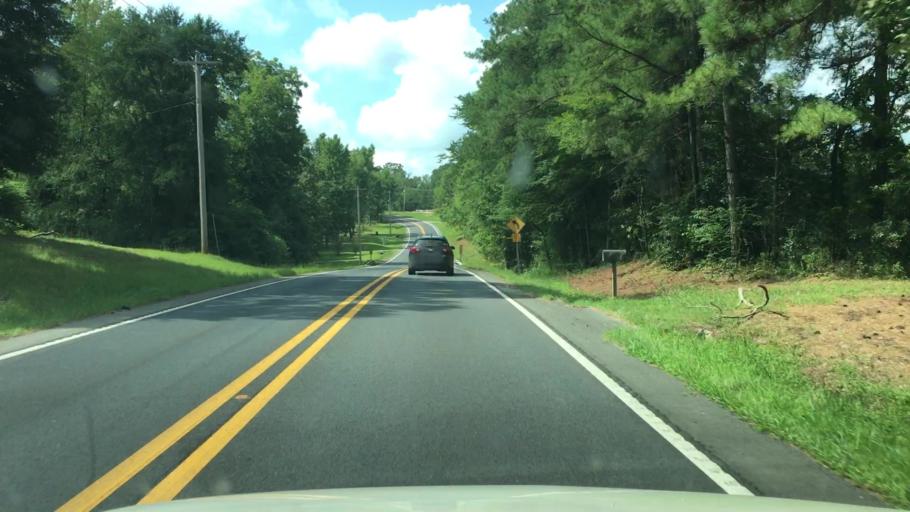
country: US
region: Arkansas
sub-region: Garland County
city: Lake Hamilton
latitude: 34.2935
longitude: -93.1627
